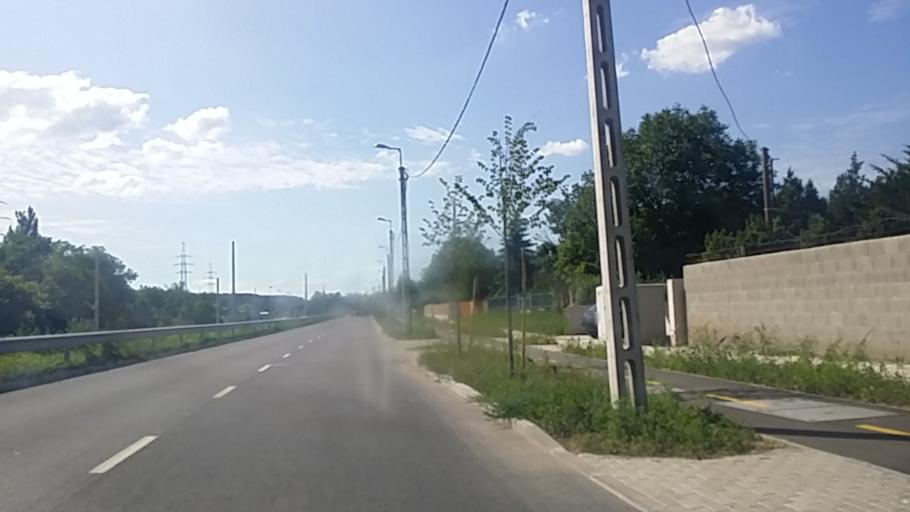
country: HU
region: Pest
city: Urom
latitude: 47.5723
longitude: 19.0214
